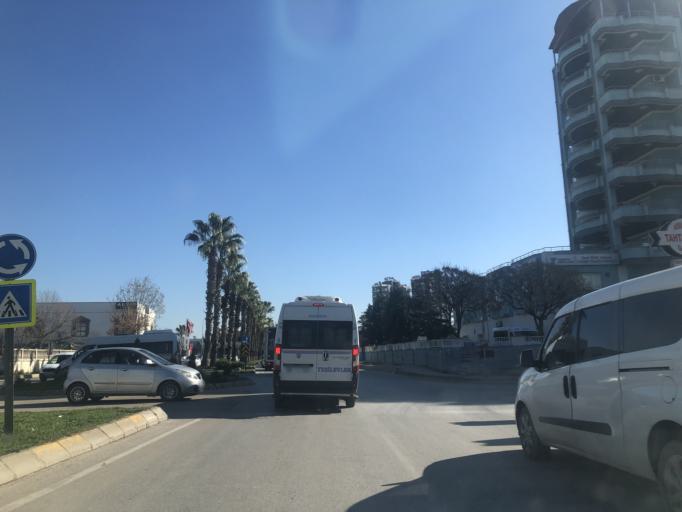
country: TR
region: Adana
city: Adana
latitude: 36.9800
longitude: 35.3367
